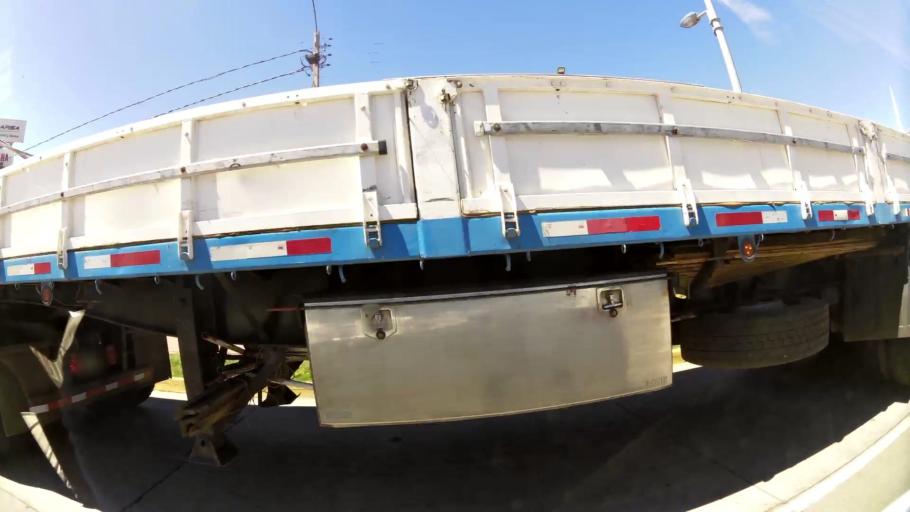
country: CL
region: Biobio
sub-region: Provincia de Concepcion
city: Talcahuano
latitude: -36.7506
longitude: -73.0931
